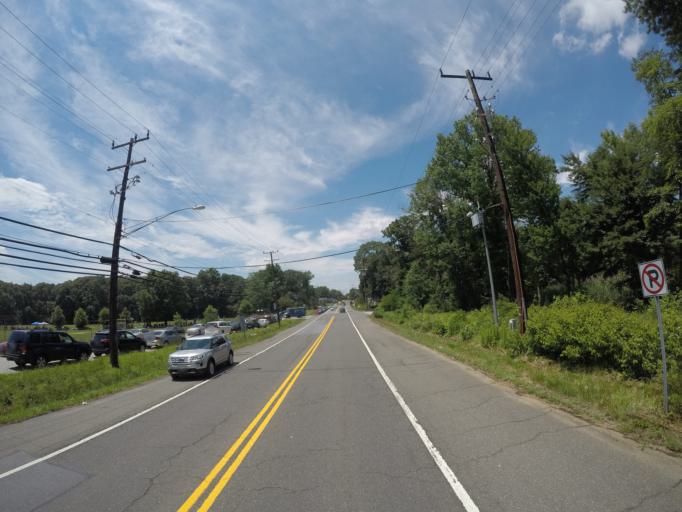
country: US
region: Maryland
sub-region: Prince George's County
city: New Carrollton
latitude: 38.9773
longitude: -76.8759
